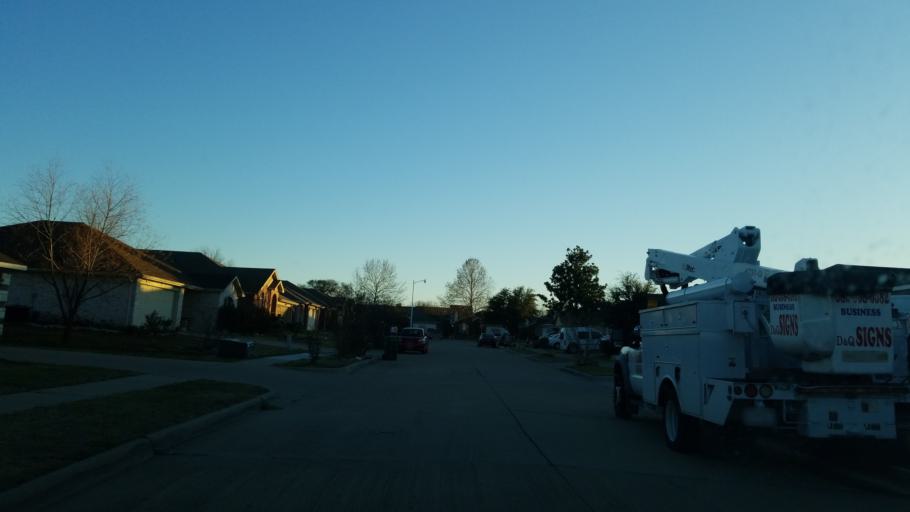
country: US
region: Texas
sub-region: Tarrant County
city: Arlington
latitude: 32.7249
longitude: -97.0531
